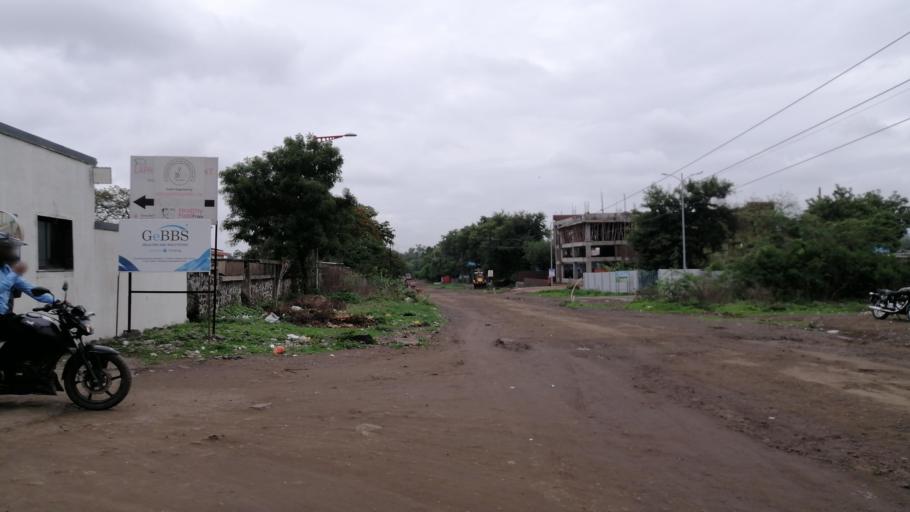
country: IN
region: Maharashtra
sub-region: Aurangabad Division
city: Aurangabad
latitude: 19.8828
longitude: 75.3783
